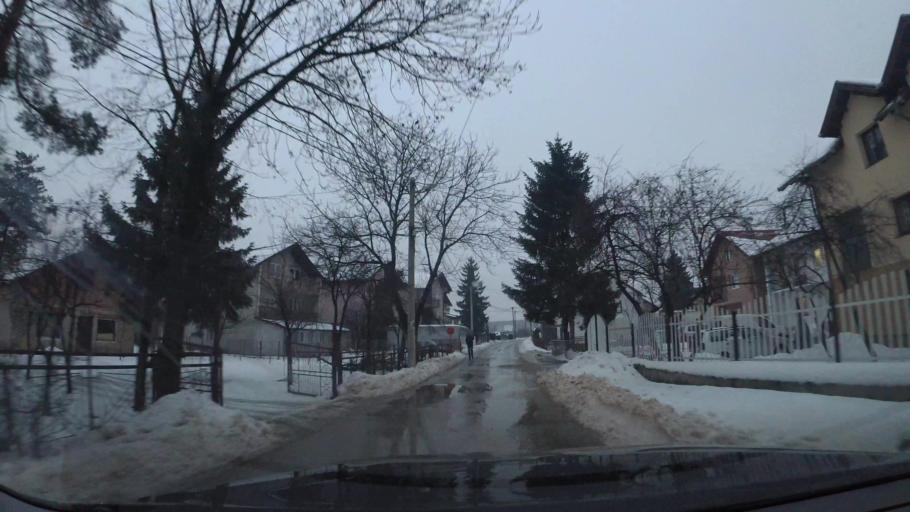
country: BA
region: Federation of Bosnia and Herzegovina
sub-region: Kanton Sarajevo
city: Sarajevo
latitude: 43.8385
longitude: 18.3018
